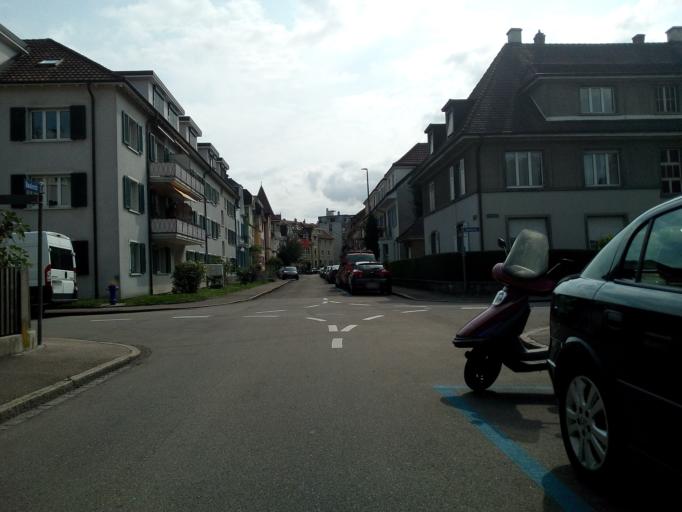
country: CH
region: Basel-Landschaft
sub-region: Bezirk Arlesheim
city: Birsfelden
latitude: 47.5567
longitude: 7.6190
